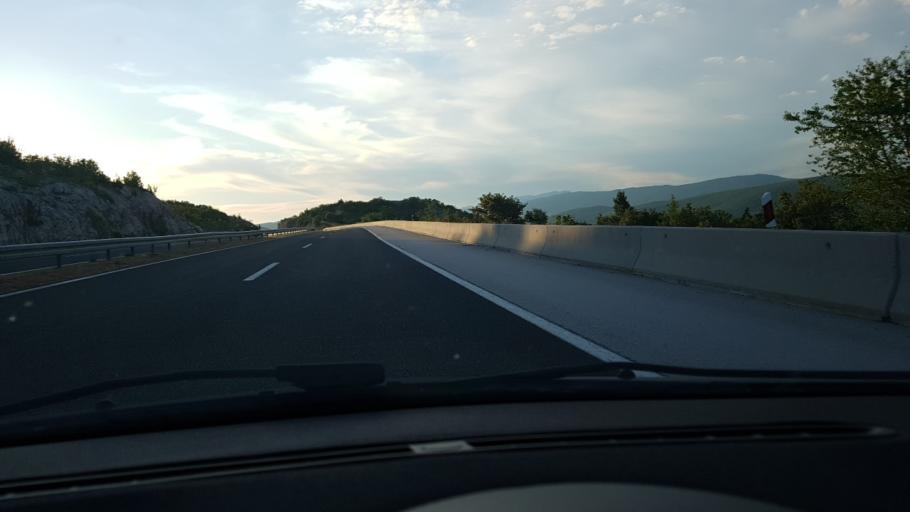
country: HR
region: Splitsko-Dalmatinska
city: Dugopolje
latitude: 43.5845
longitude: 16.6430
